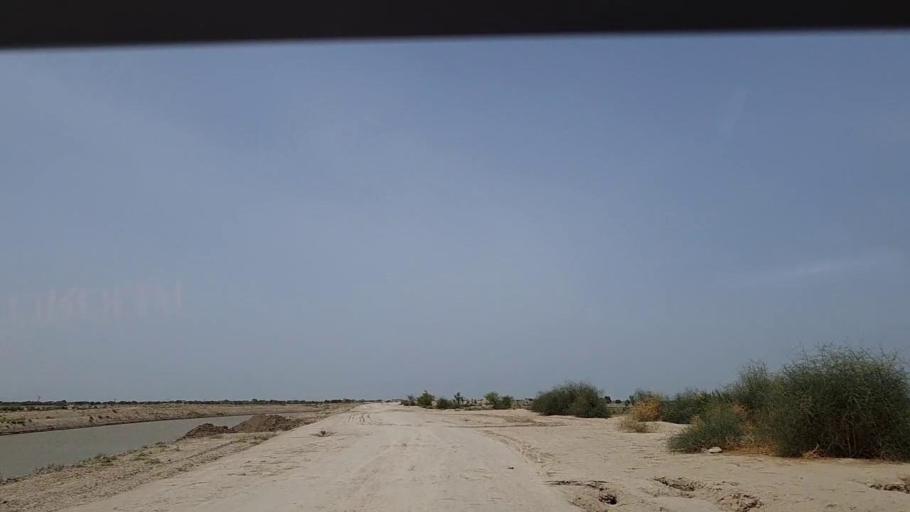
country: PK
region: Sindh
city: Johi
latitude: 26.7314
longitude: 67.6826
